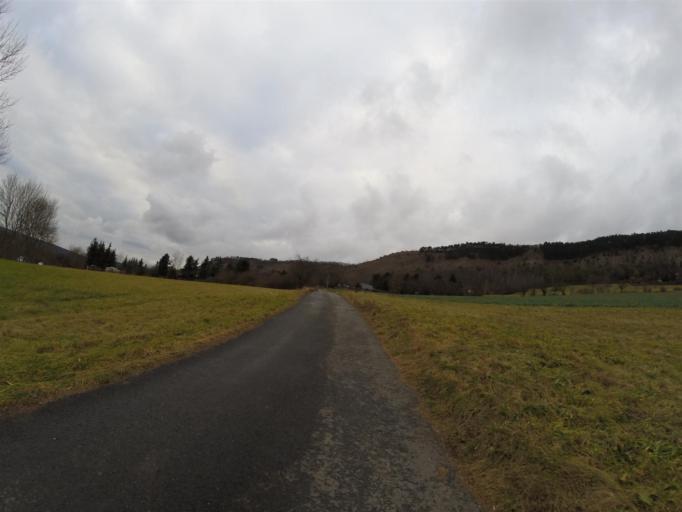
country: DE
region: Thuringia
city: Golmsdorf
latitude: 50.9334
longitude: 11.6386
